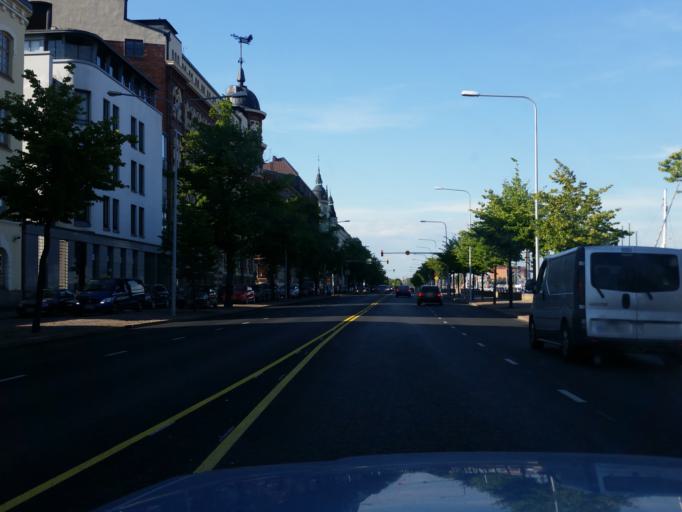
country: FI
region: Uusimaa
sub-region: Helsinki
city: Helsinki
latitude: 60.1700
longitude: 24.9598
